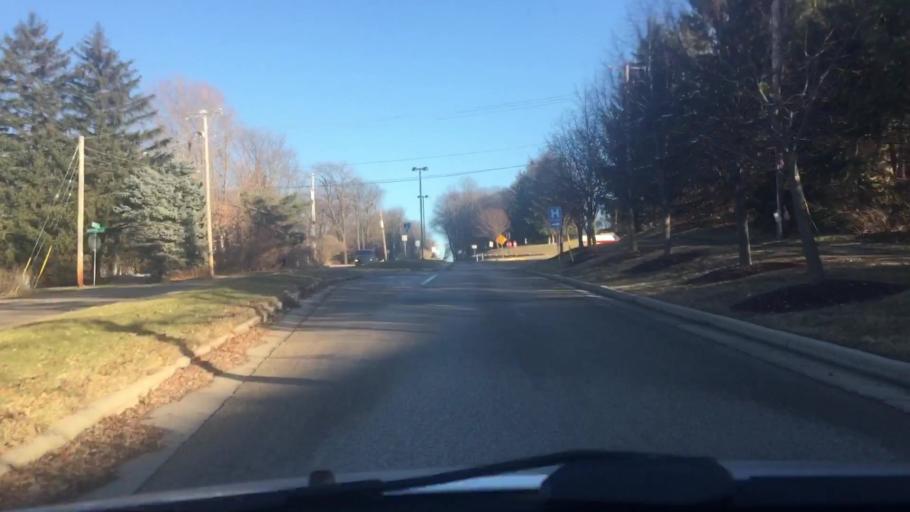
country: US
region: Wisconsin
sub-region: Waukesha County
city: Brookfield
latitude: 43.0613
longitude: -88.1544
